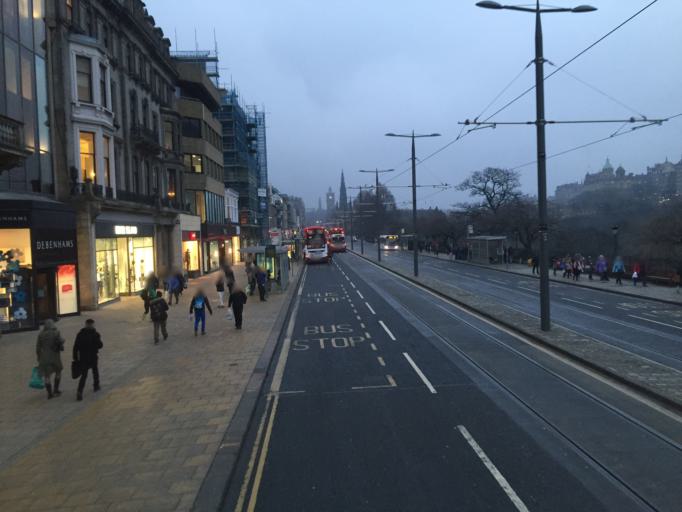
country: GB
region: Scotland
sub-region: Edinburgh
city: Edinburgh
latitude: 55.9512
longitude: -3.2017
